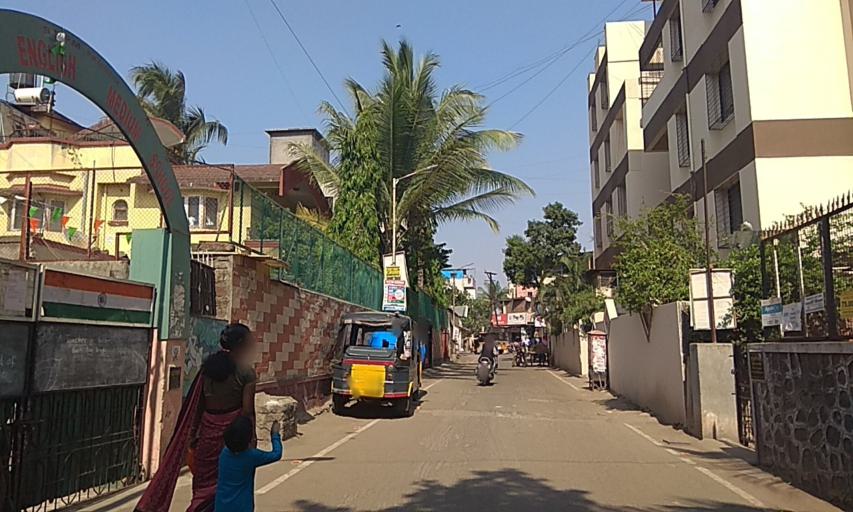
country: IN
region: Maharashtra
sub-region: Pune Division
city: Lohogaon
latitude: 18.5532
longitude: 73.9357
